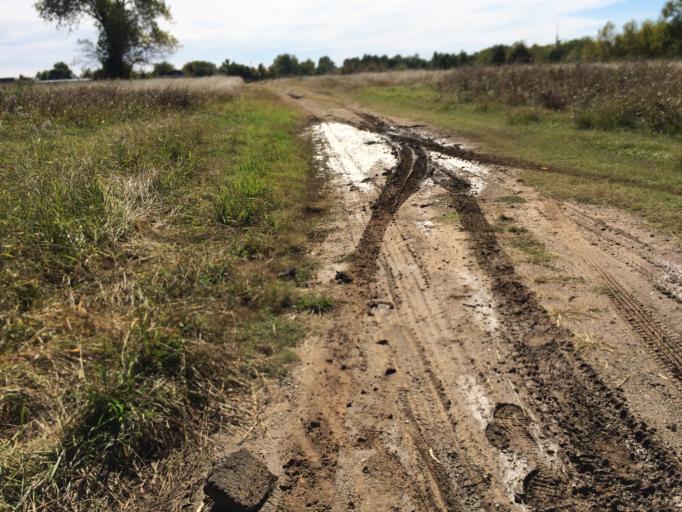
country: US
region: Oklahoma
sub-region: Cleveland County
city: Norman
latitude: 35.2220
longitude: -97.4284
